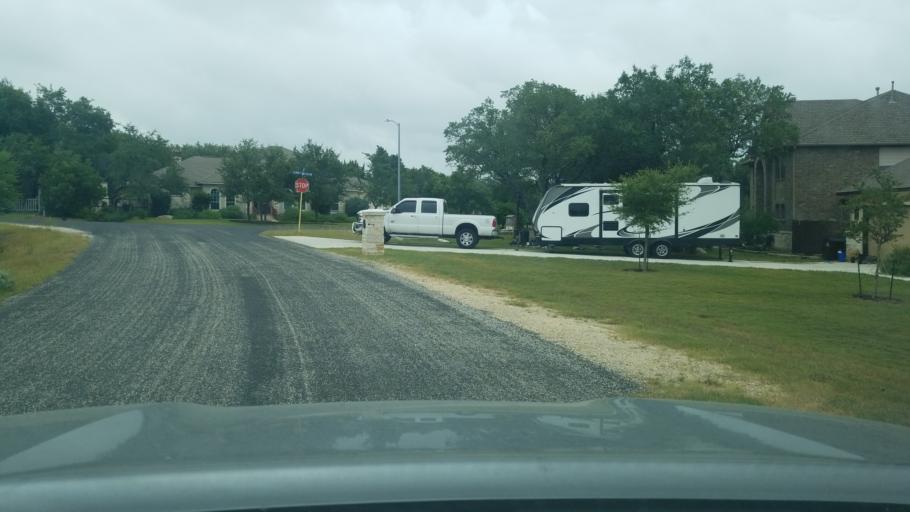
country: US
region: Texas
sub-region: Bexar County
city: Timberwood Park
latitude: 29.7016
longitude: -98.5107
